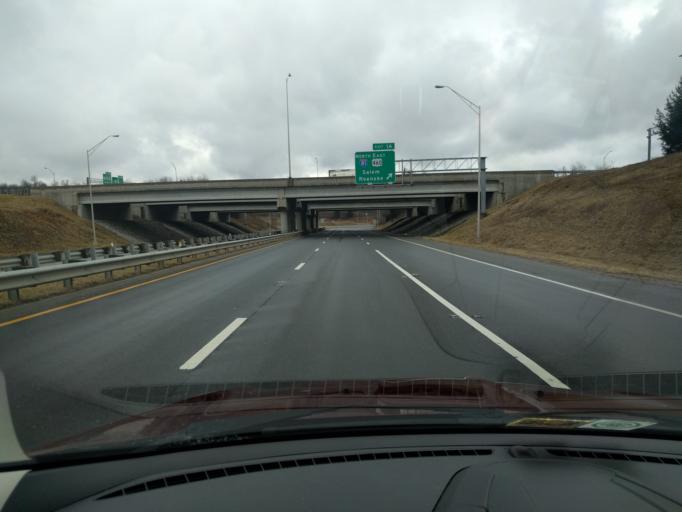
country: US
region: Virginia
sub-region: Montgomery County
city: Christiansburg
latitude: 37.1300
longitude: -80.3709
